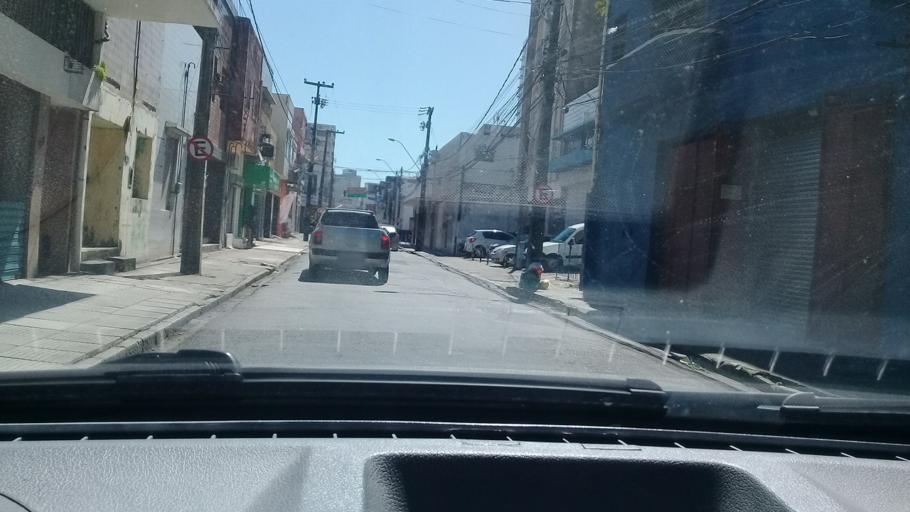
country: BR
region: Pernambuco
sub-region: Recife
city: Recife
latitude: -8.0717
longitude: -34.8844
